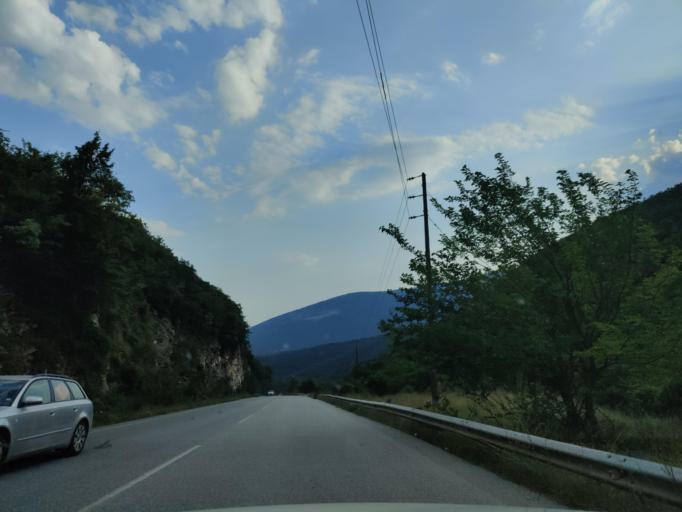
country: GR
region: East Macedonia and Thrace
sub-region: Nomos Dramas
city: Volakas
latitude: 41.2732
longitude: 23.9765
